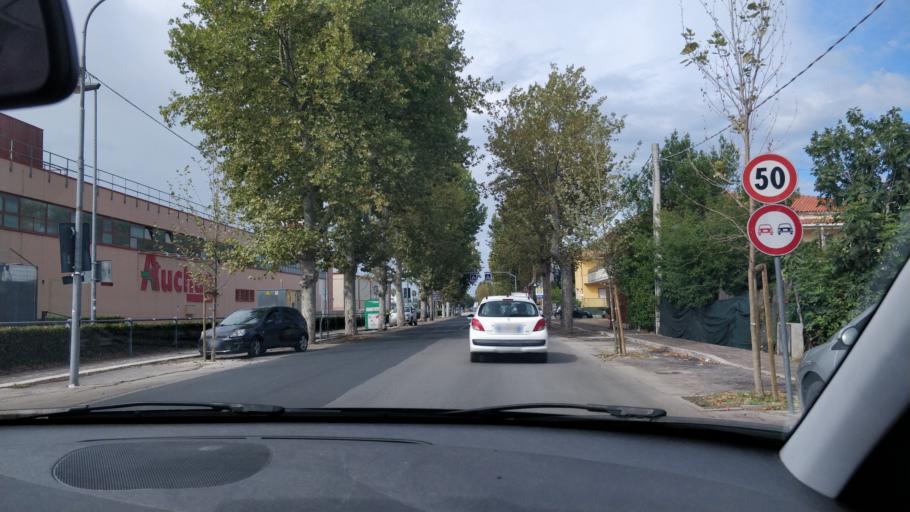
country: IT
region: Abruzzo
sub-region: Provincia di Chieti
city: Sambuceto
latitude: 42.4261
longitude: 14.1861
